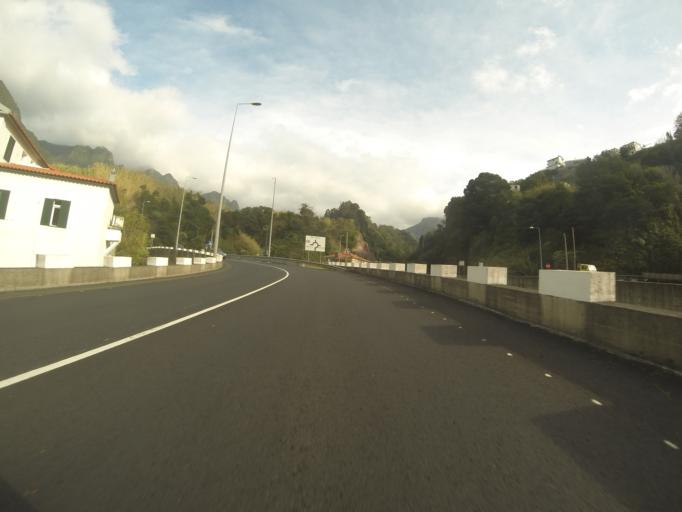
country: PT
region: Madeira
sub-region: Sao Vicente
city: Sao Vicente
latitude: 32.7924
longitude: -17.0352
